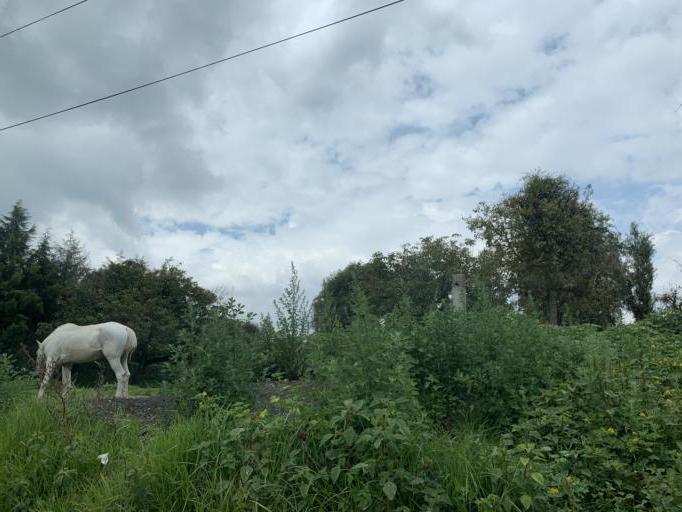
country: MX
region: Puebla
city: Huejotzingo
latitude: 19.1503
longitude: -98.4021
